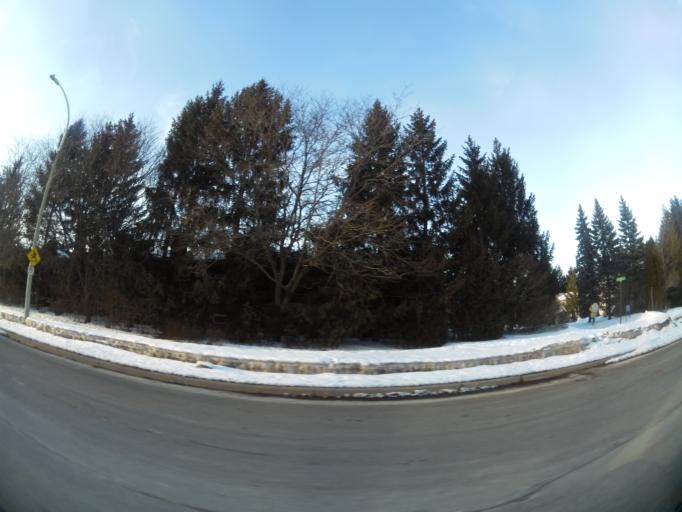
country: CA
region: Ontario
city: Ottawa
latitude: 45.4495
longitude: -75.5279
